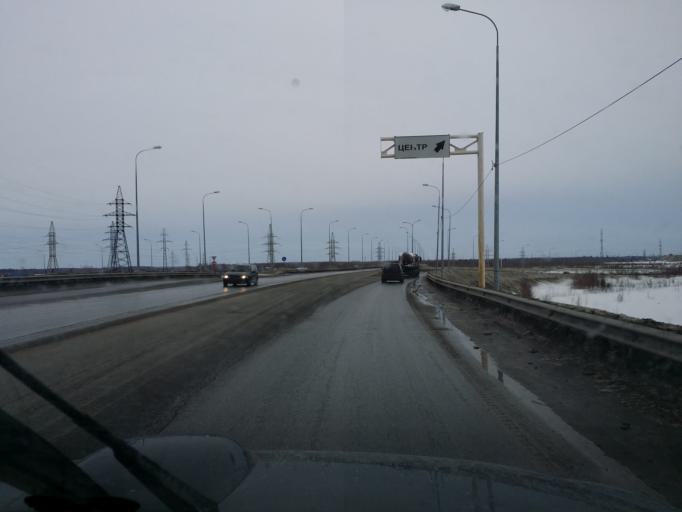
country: RU
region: Khanty-Mansiyskiy Avtonomnyy Okrug
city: Nizhnevartovsk
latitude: 60.9503
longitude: 76.6635
